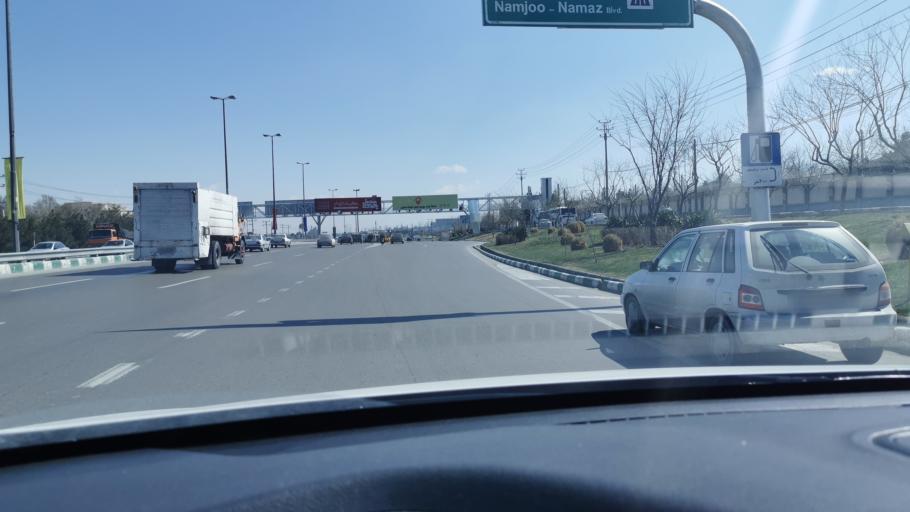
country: IR
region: Razavi Khorasan
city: Mashhad
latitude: 36.2718
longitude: 59.5712
